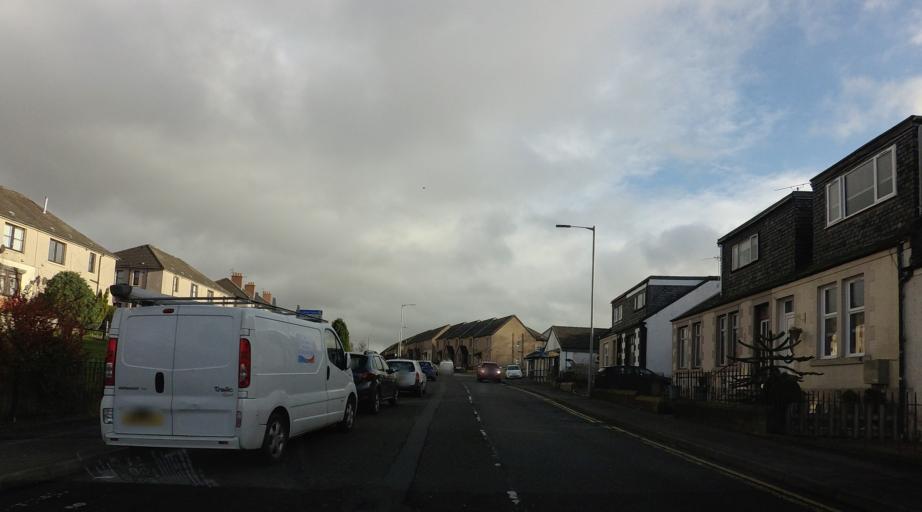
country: GB
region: Scotland
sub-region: Falkirk
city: Polmont
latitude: 55.9750
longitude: -3.7093
